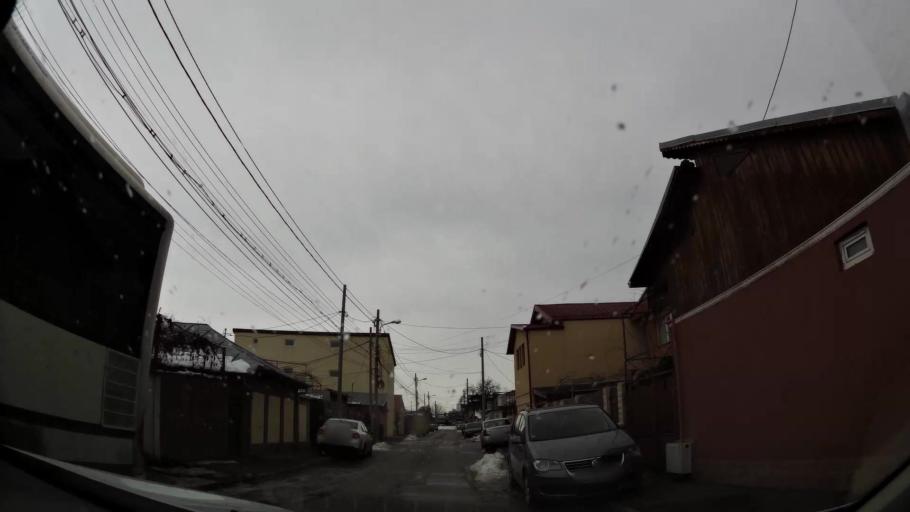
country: RO
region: Ilfov
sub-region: Comuna Pantelimon
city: Pantelimon
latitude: 44.4309
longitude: 26.2047
